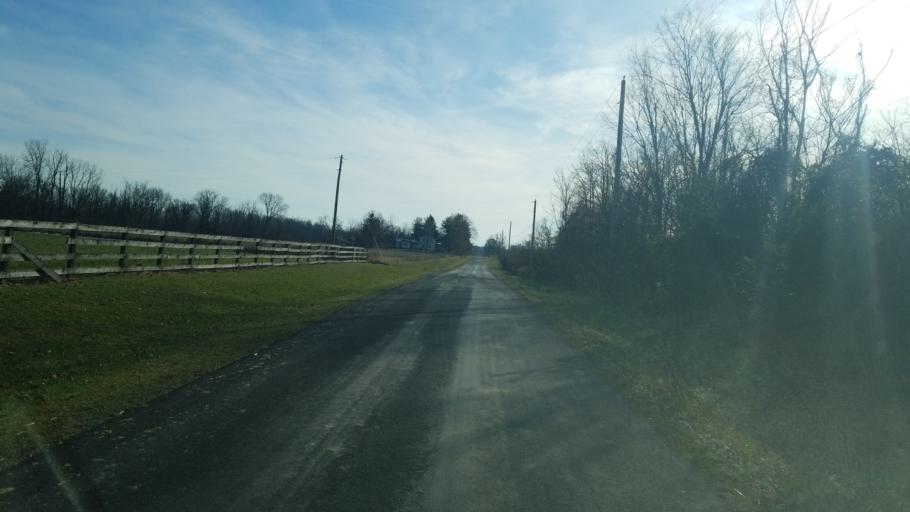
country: US
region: Ohio
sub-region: Lorain County
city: Wellington
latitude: 41.0832
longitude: -82.2589
